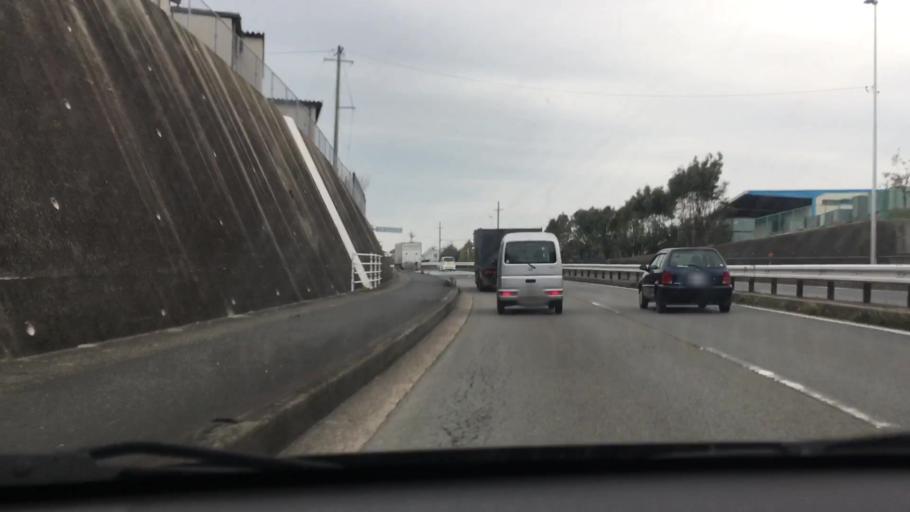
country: JP
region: Mie
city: Suzuka
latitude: 34.8993
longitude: 136.5484
